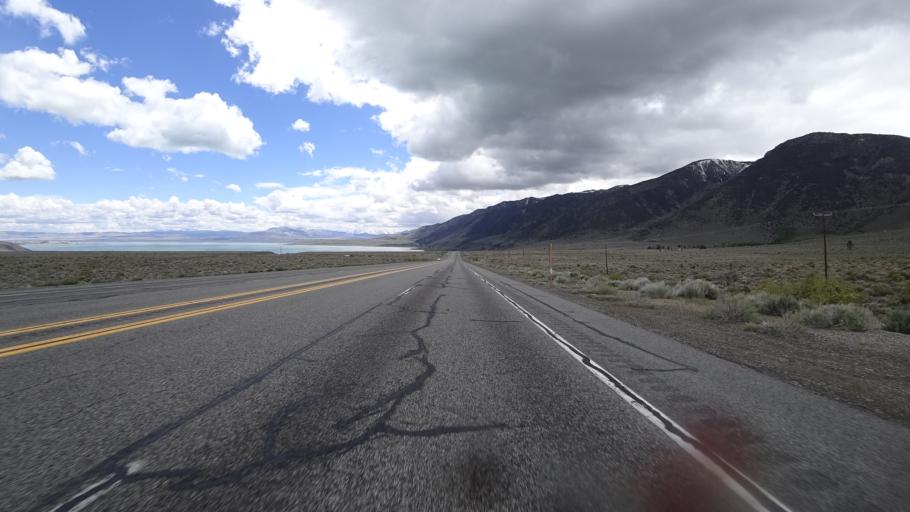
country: US
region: California
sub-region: Mono County
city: Bridgeport
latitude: 38.0340
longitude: -119.1572
